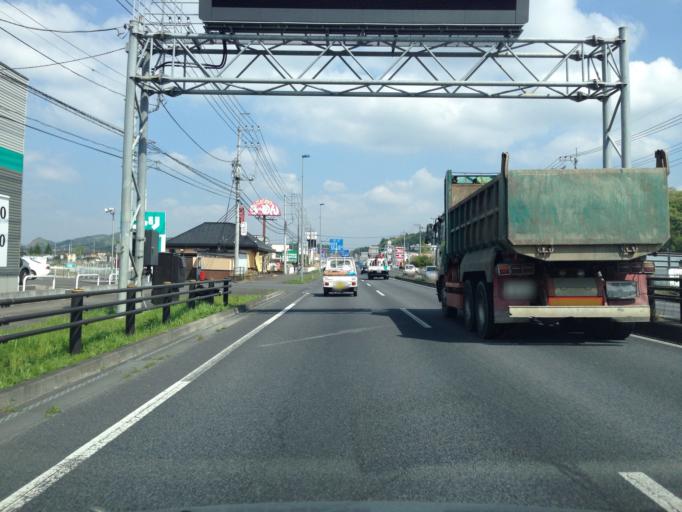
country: JP
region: Ibaraki
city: Kasama
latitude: 36.3937
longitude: 140.2560
